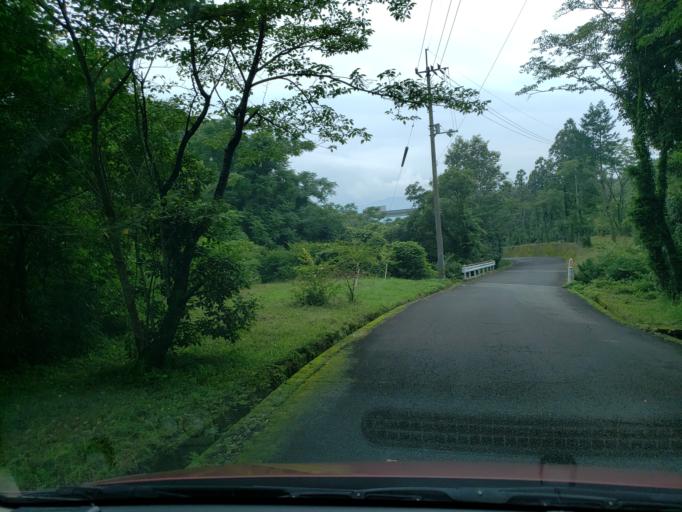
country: JP
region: Tokushima
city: Kamojimacho-jogejima
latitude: 34.1068
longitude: 134.2980
